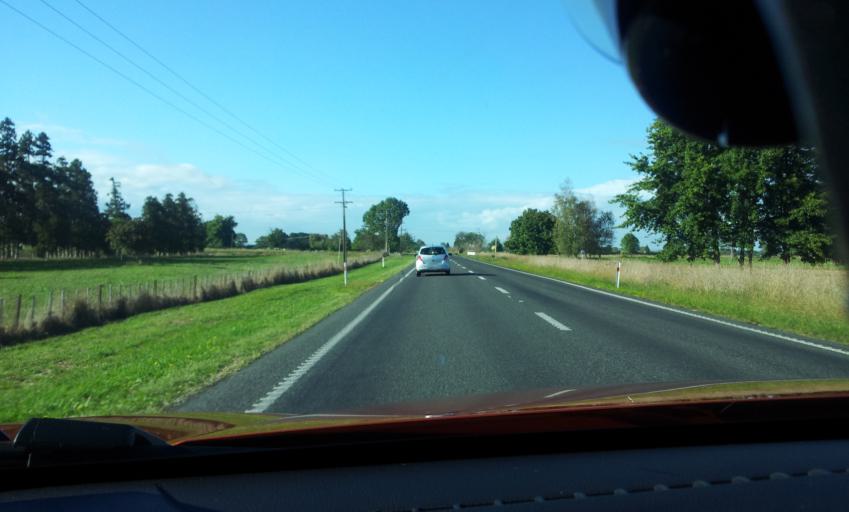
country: NZ
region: Waikato
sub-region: Hauraki District
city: Paeroa
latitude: -37.4918
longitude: 175.5205
